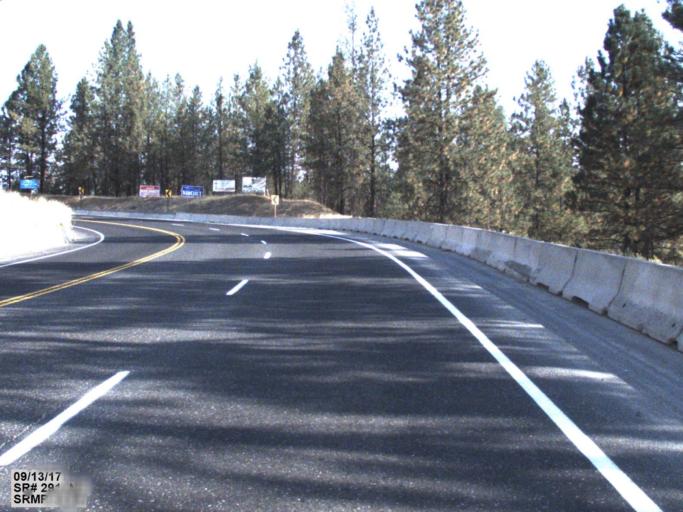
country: US
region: Washington
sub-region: Spokane County
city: Fairwood
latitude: 47.8090
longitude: -117.5545
